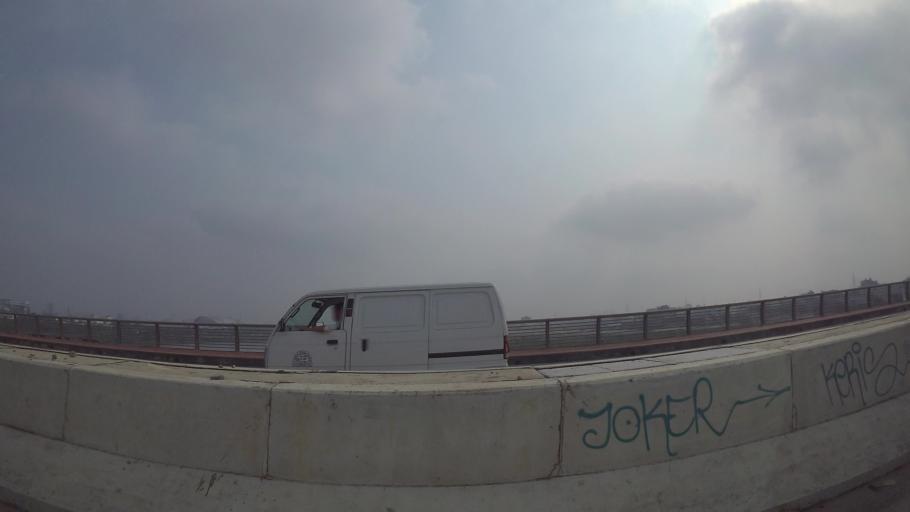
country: VN
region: Da Nang
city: Cam Le
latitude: 16.0153
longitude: 108.2141
